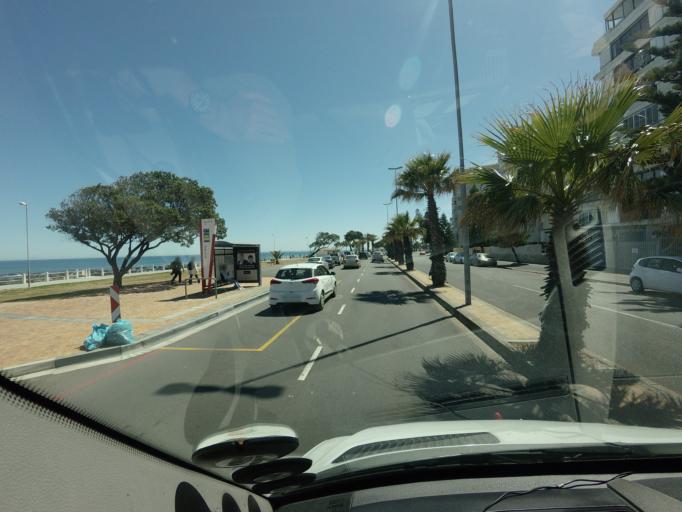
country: ZA
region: Western Cape
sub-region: City of Cape Town
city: Cape Town
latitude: -33.9164
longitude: 18.3865
